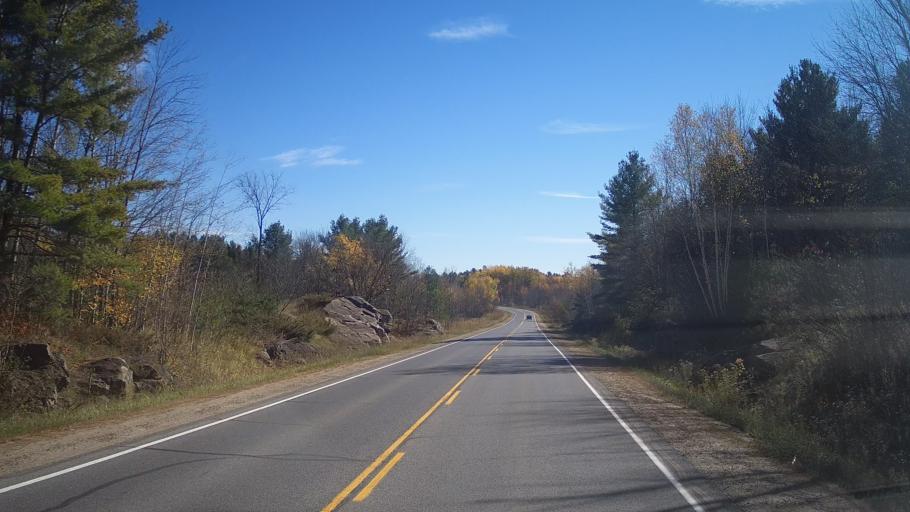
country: CA
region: Ontario
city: Skatepark
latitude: 44.6379
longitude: -76.7151
